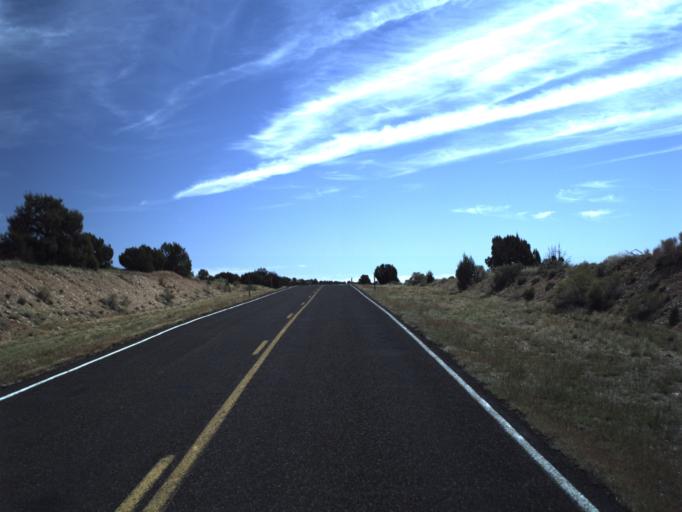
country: US
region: Utah
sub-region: Wayne County
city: Loa
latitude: 37.7395
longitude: -111.5514
